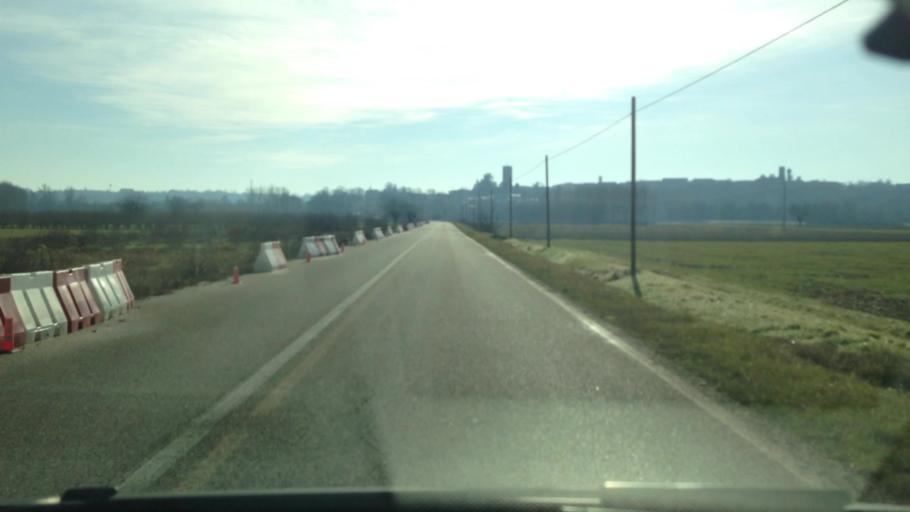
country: IT
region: Piedmont
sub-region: Provincia di Alessandria
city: Masio
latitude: 44.8794
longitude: 8.4092
